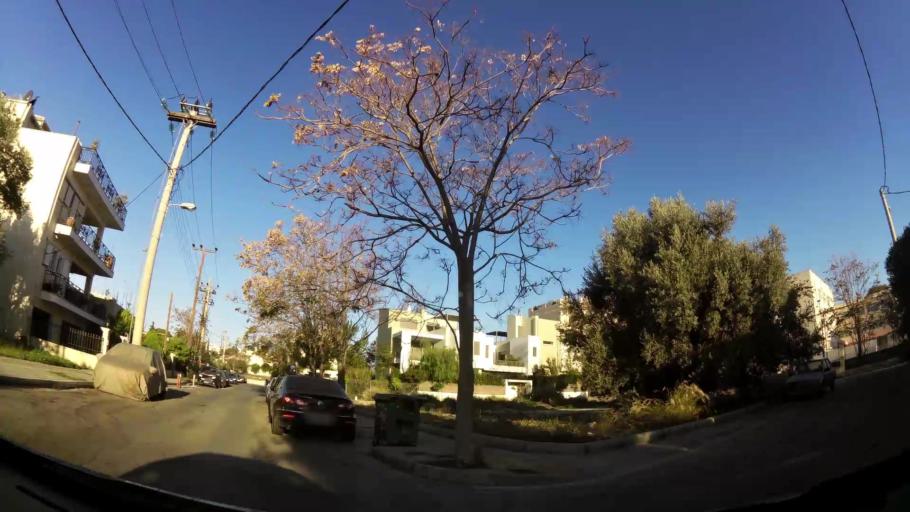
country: GR
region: Attica
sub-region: Nomarchia Athinas
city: Marousi
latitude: 38.0457
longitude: 23.7956
